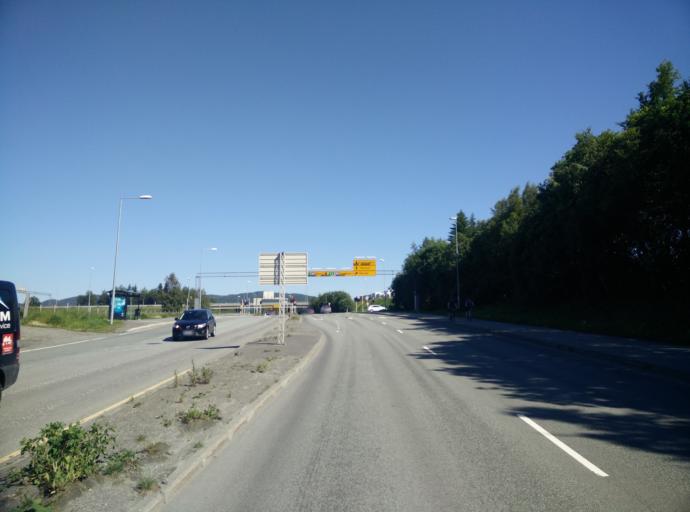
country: NO
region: Sor-Trondelag
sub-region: Trondheim
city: Trondheim
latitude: 63.3704
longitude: 10.3741
